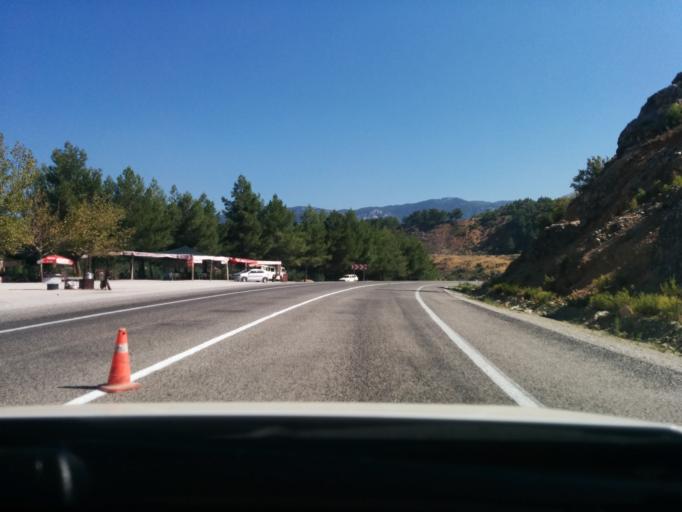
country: TR
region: Mugla
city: Kemer
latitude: 36.7205
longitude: 29.4428
